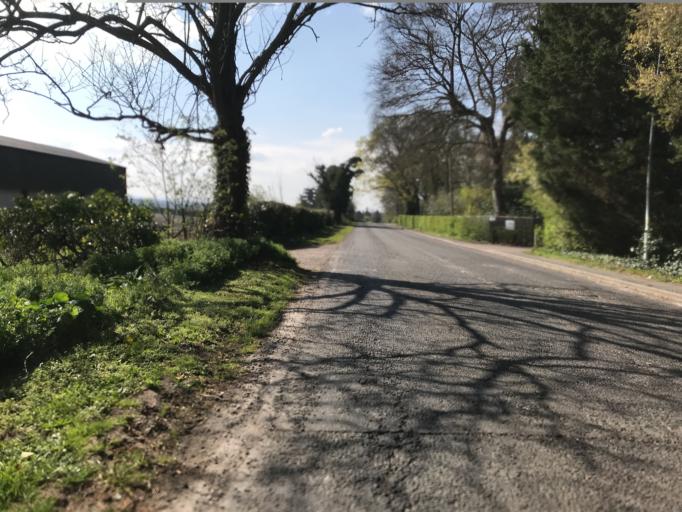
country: GB
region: England
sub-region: Cambridgeshire
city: Sawston
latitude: 52.1586
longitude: 0.1552
